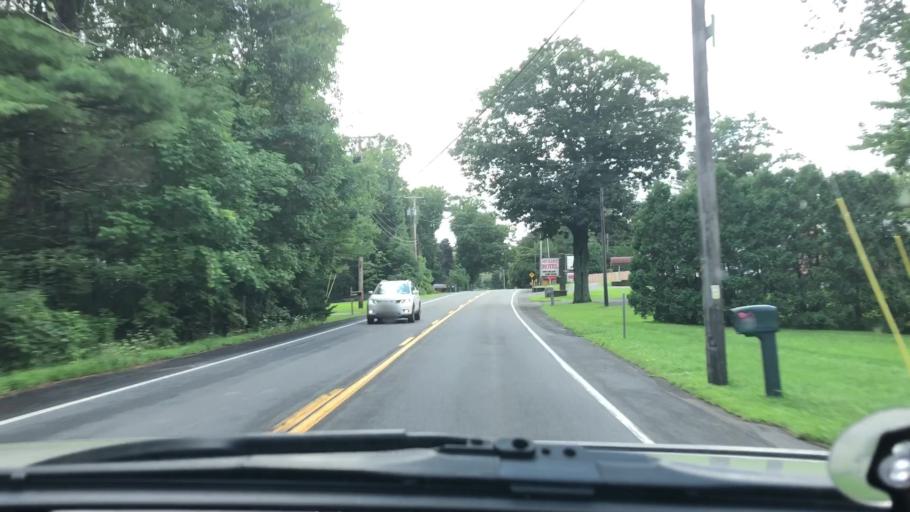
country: US
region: New York
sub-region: Greene County
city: Palenville
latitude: 42.1865
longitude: -73.9854
